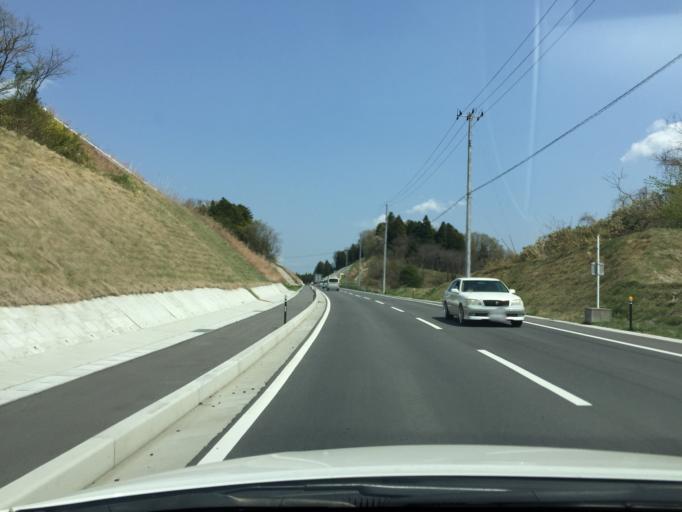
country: JP
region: Fukushima
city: Funehikimachi-funehiki
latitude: 37.4392
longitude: 140.5428
